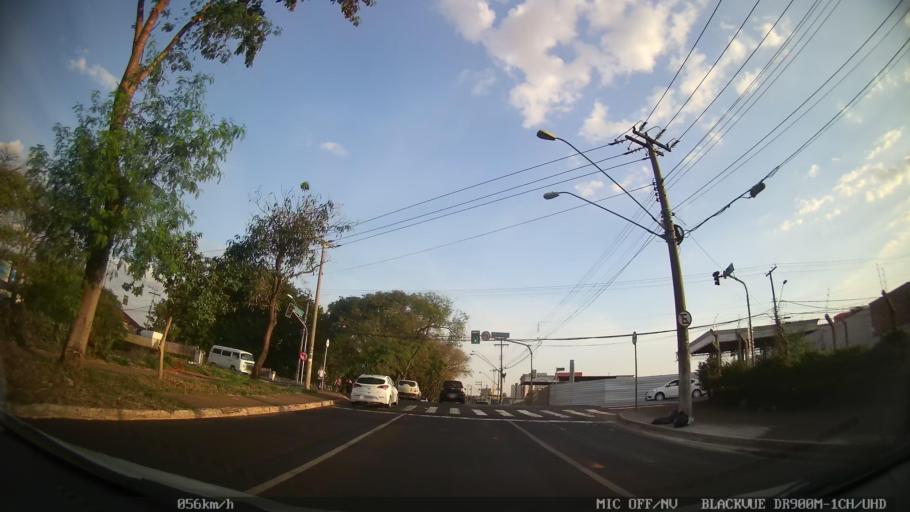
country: BR
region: Sao Paulo
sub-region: Ribeirao Preto
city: Ribeirao Preto
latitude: -21.1527
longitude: -47.8094
